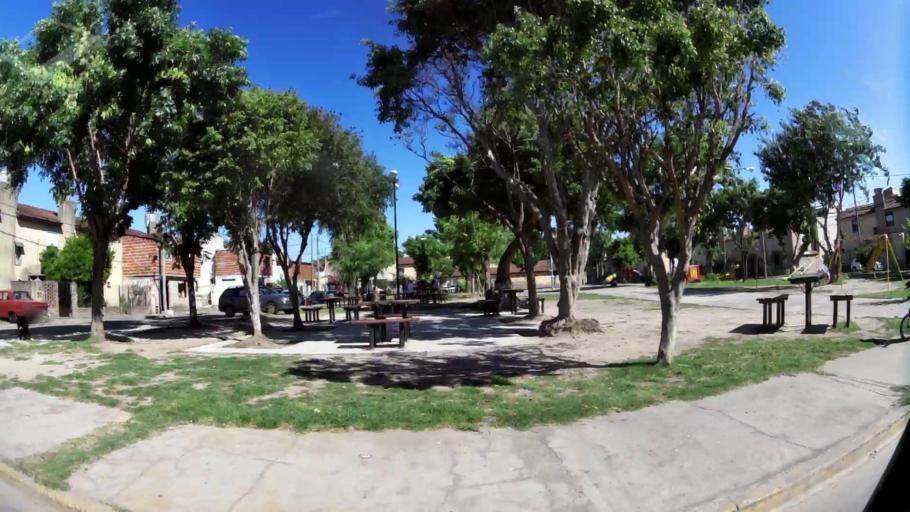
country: AR
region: Buenos Aires
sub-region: Partido de San Isidro
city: San Isidro
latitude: -34.4690
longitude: -58.5330
